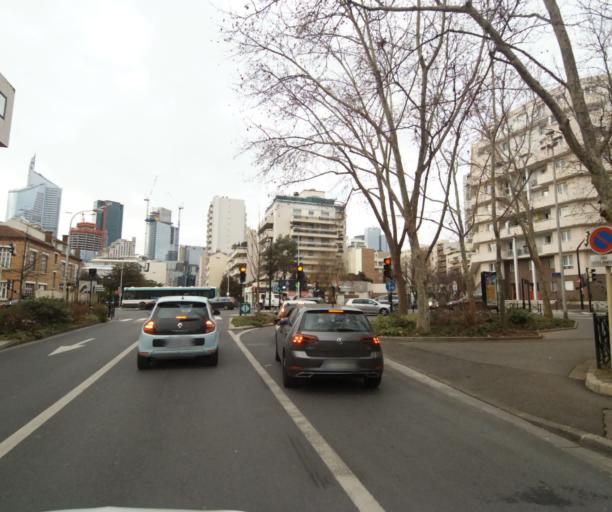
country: FR
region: Ile-de-France
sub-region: Departement des Hauts-de-Seine
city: Courbevoie
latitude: 48.8940
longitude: 2.2571
